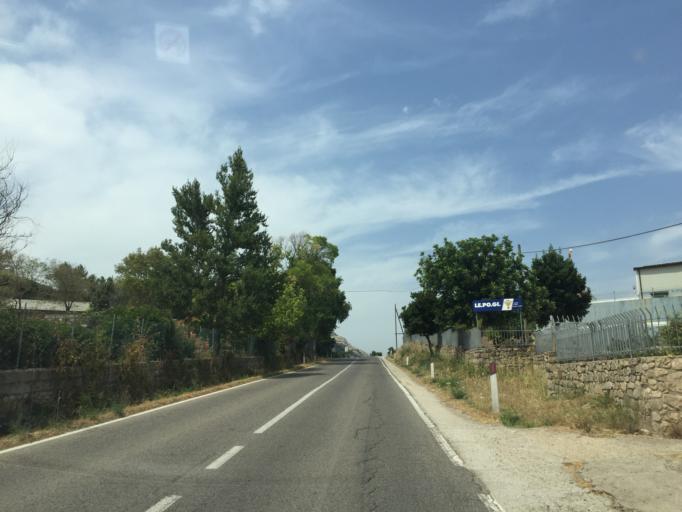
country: IT
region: Sardinia
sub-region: Provincia di Olbia-Tempio
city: Aggius
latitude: 40.9214
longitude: 9.0714
